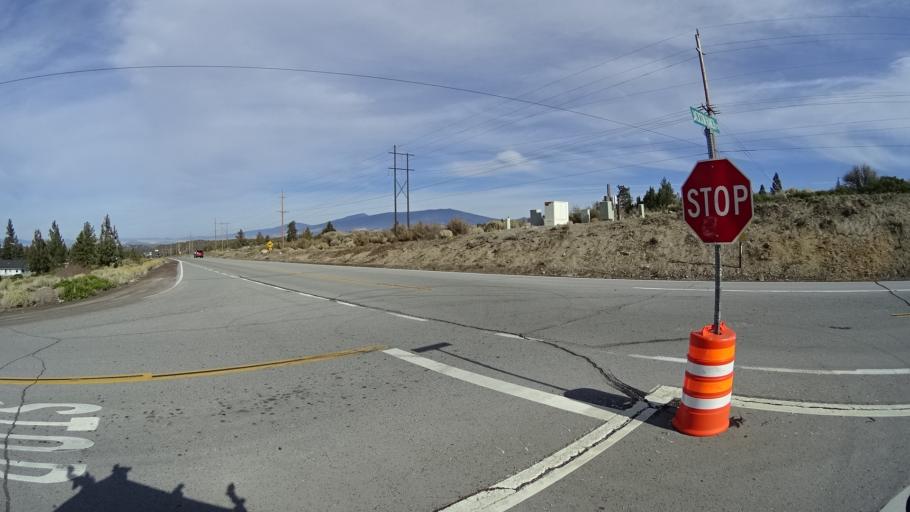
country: US
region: California
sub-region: Siskiyou County
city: Weed
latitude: 41.4939
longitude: -122.3626
